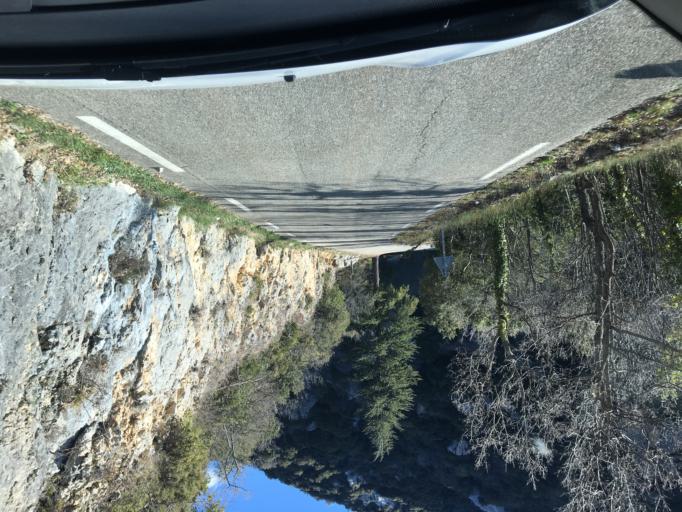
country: FR
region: Provence-Alpes-Cote d'Azur
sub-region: Departement du Vaucluse
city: Villes-sur-Auzon
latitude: 44.0676
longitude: 5.3218
